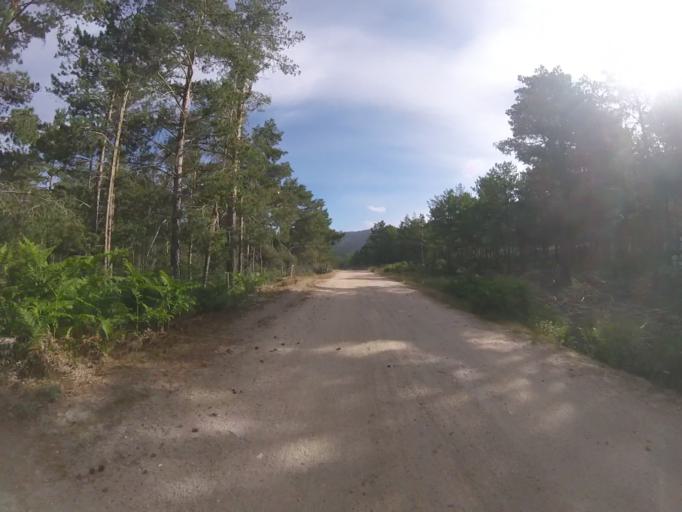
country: ES
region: Castille and Leon
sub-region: Provincia de Avila
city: Peguerinos
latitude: 40.6611
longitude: -4.1836
